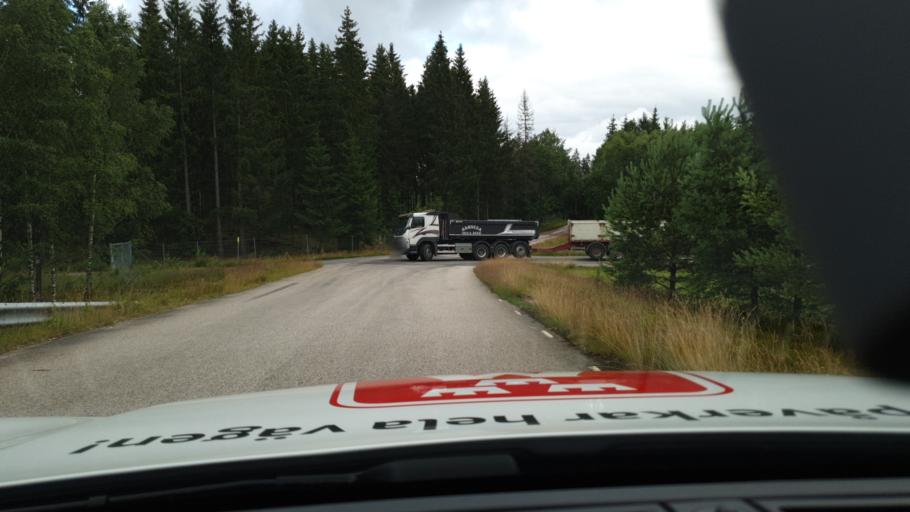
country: SE
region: Kronoberg
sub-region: Markaryds Kommun
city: Stromsnasbruk
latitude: 56.6160
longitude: 13.7601
